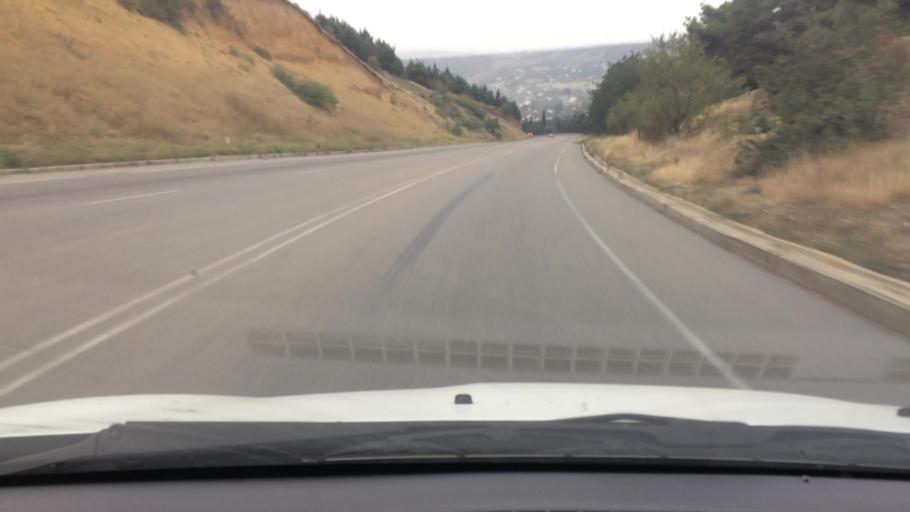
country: GE
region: T'bilisi
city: Tbilisi
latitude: 41.6255
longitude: 44.8052
